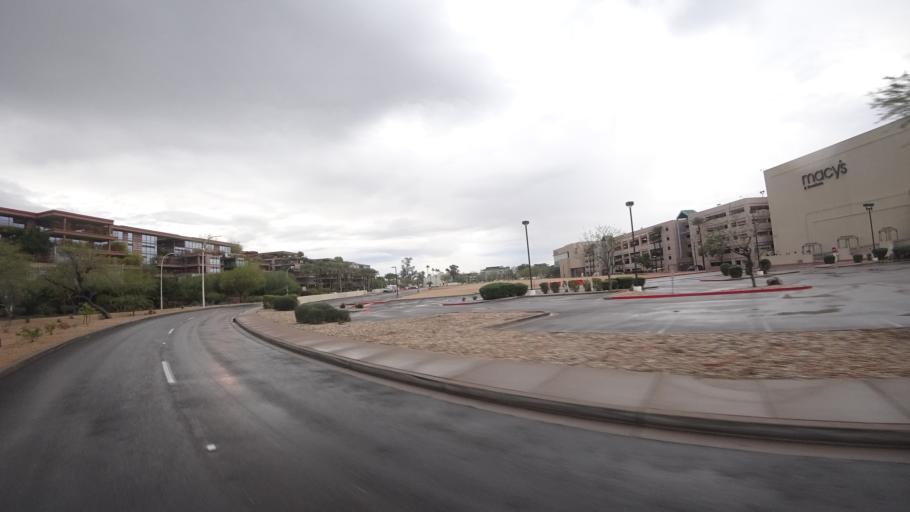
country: US
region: Arizona
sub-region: Maricopa County
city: Paradise Valley
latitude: 33.5055
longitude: -111.9301
